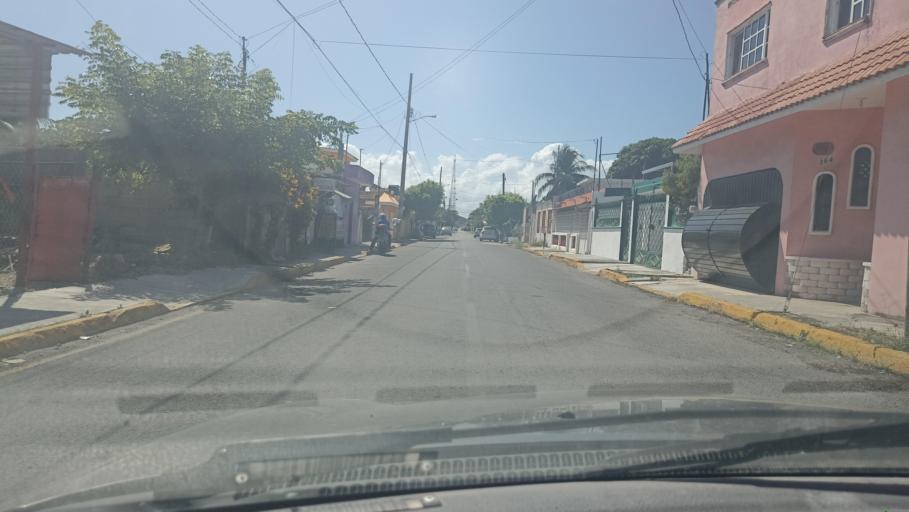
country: MX
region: Quintana Roo
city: Chetumal
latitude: 18.5118
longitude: -88.2879
